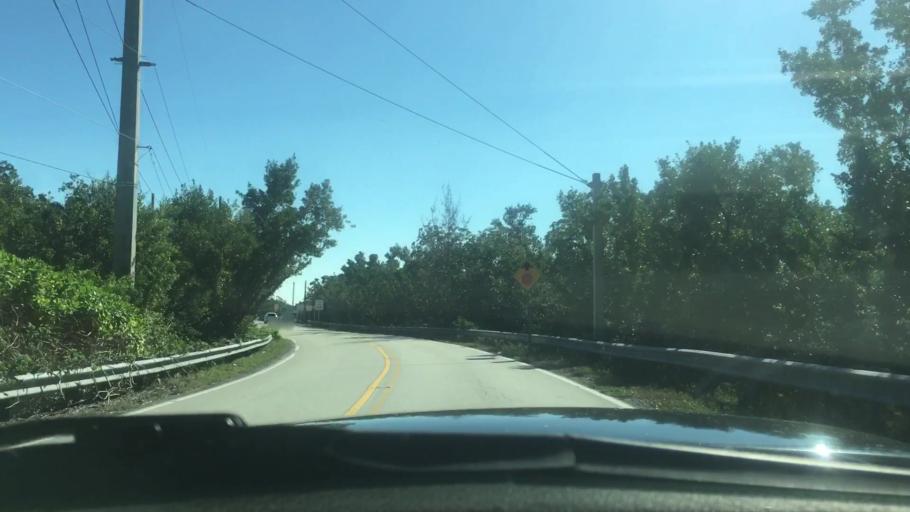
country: US
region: Florida
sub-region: Monroe County
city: North Key Largo
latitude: 25.2927
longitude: -80.3812
